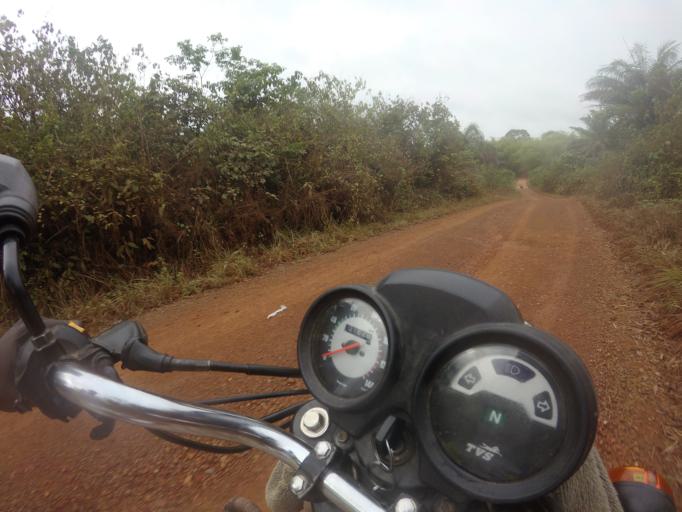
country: SL
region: Southern Province
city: Zimmi
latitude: 7.2123
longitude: -11.1975
